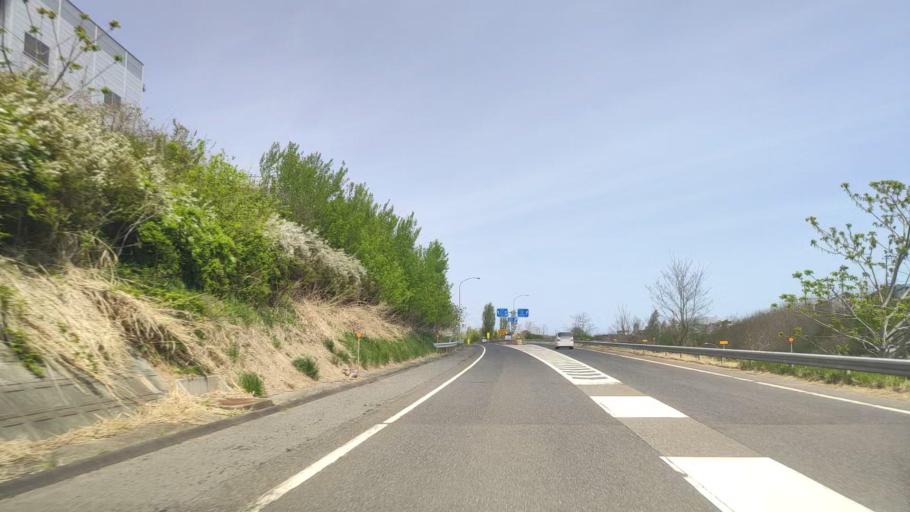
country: JP
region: Aomori
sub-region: Hachinohe Shi
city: Uchimaru
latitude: 40.4912
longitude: 141.4645
